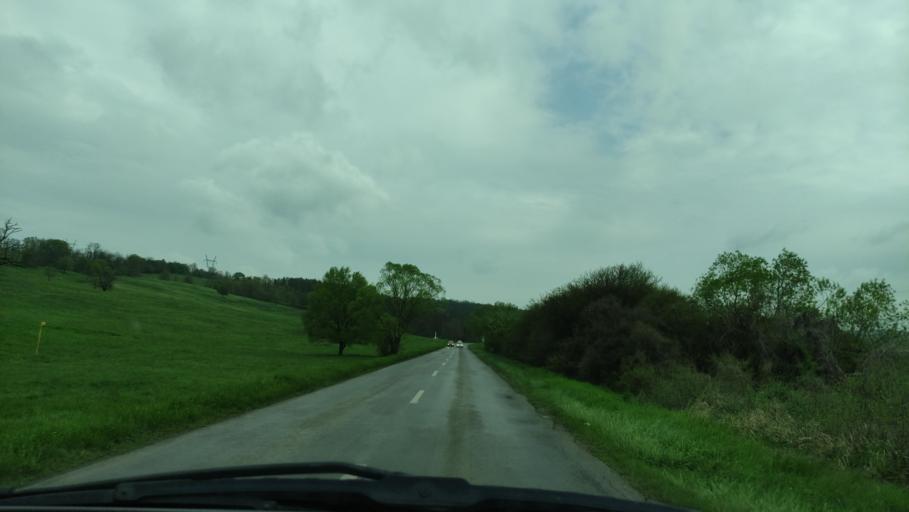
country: HU
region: Baranya
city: Komlo
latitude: 46.2141
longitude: 18.1934
